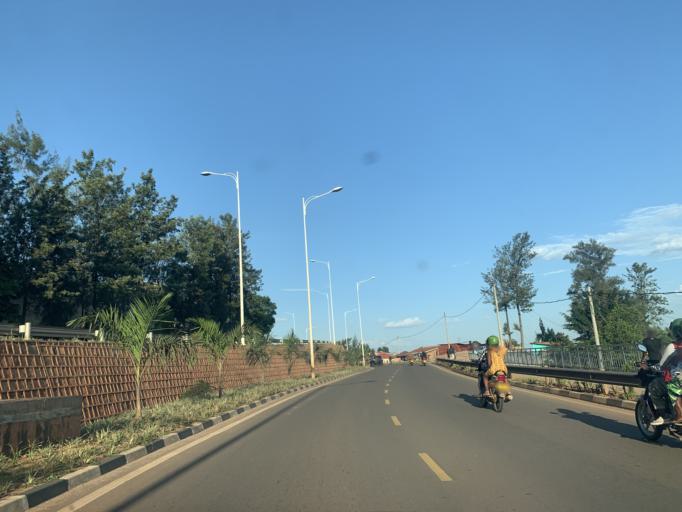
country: RW
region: Kigali
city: Kigali
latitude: -1.9651
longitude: 30.1041
